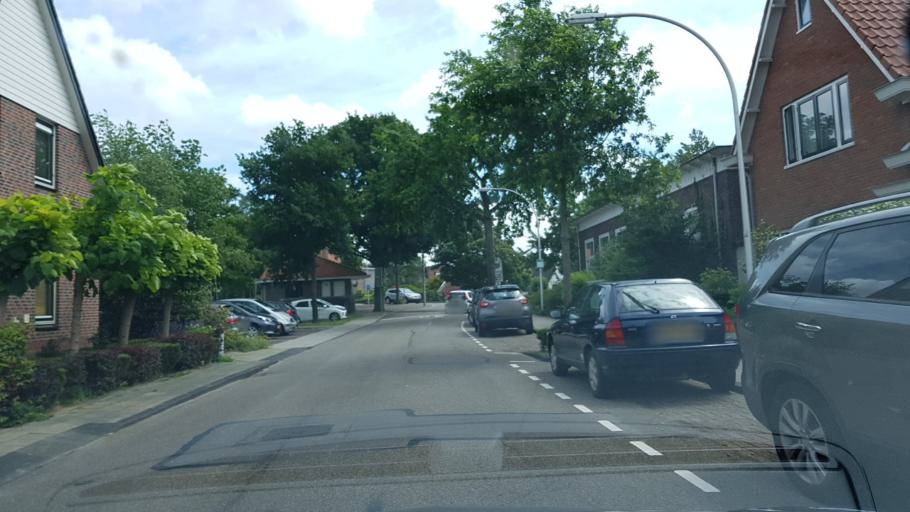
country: NL
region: North Holland
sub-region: Gemeente Bloemendaal
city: Bennebroek
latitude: 52.3300
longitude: 4.6081
